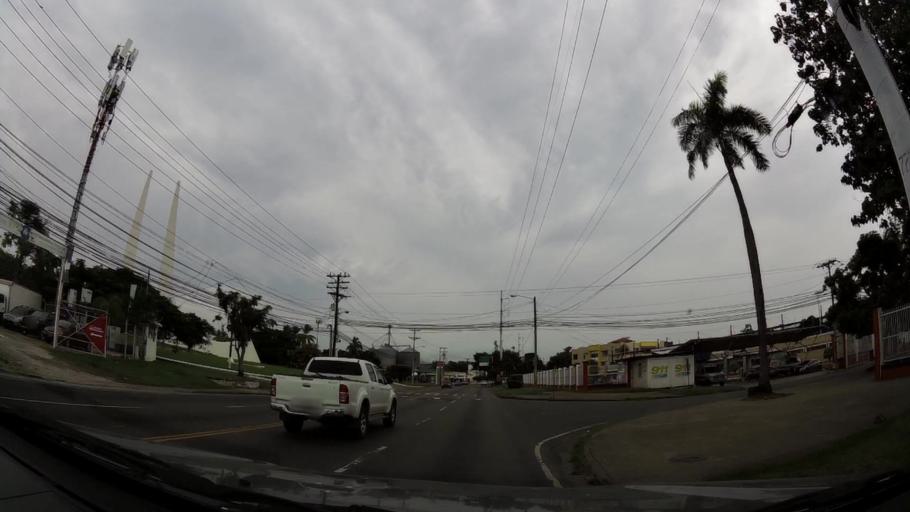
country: PA
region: Panama
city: San Miguelito
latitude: 9.0346
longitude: -79.4728
